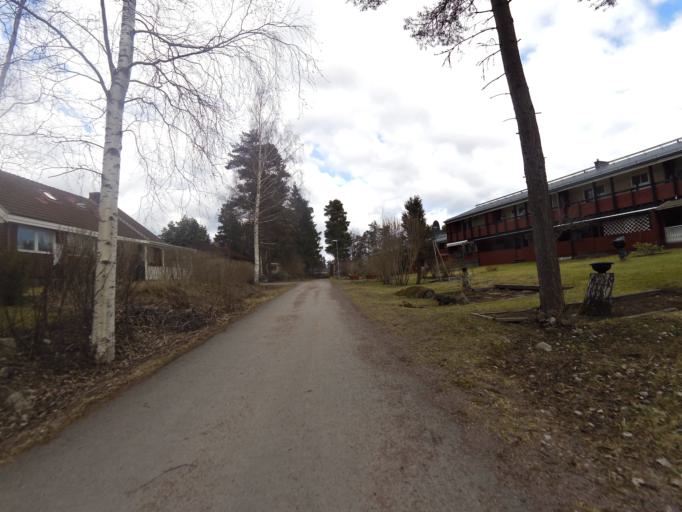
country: SE
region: Gaevleborg
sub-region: Gavle Kommun
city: Gavle
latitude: 60.6943
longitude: 17.0992
